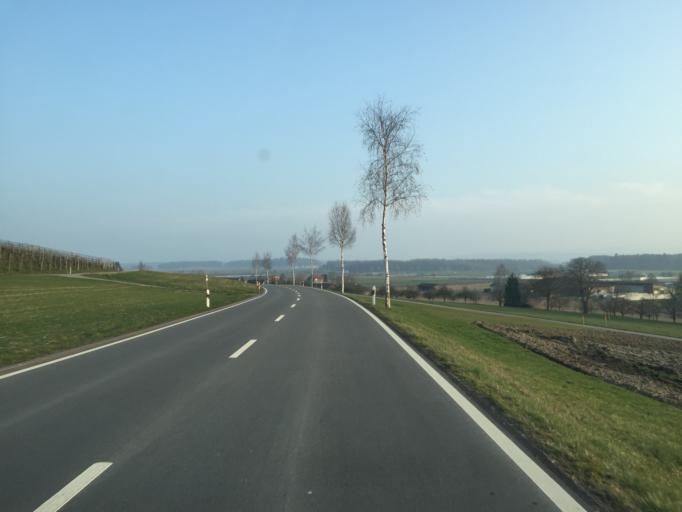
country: CH
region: Zurich
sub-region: Bezirk Andelfingen
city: Uhwiesen
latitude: 47.6571
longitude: 8.6449
